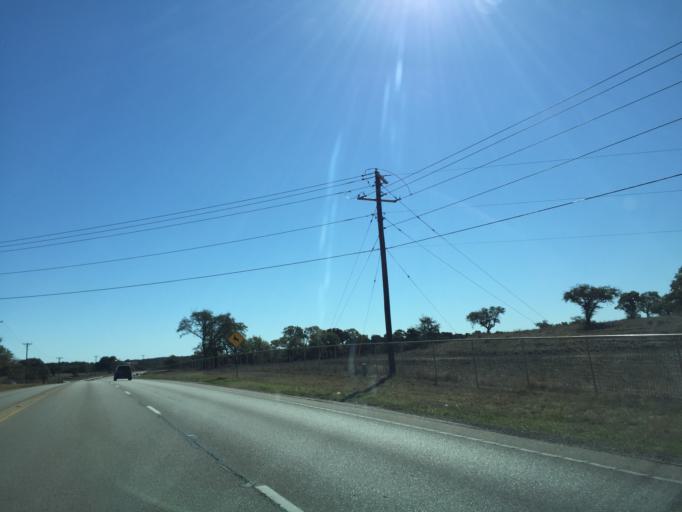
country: US
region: Texas
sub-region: Comal County
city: Canyon Lake
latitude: 29.7835
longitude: -98.3226
